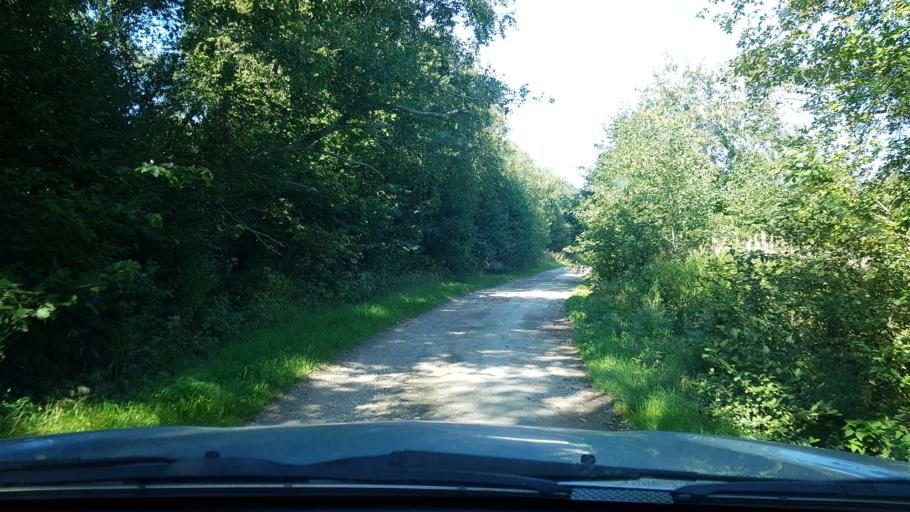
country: EE
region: Ida-Virumaa
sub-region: Sillamaee linn
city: Sillamae
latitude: 59.3941
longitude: 27.8776
